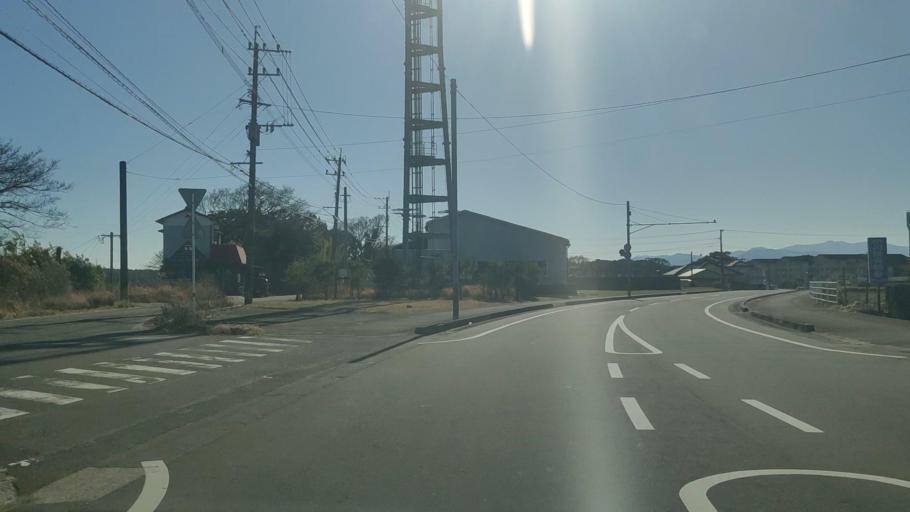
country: JP
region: Miyazaki
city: Miyazaki-shi
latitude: 31.9553
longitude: 131.4628
